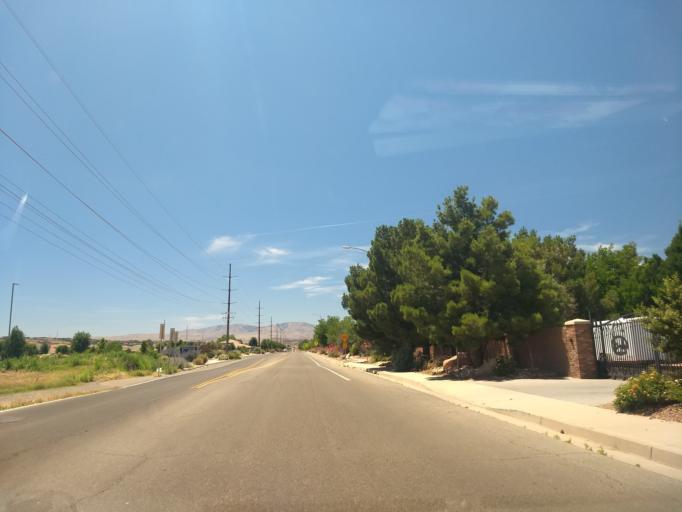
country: US
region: Utah
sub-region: Washington County
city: Washington
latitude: 37.0889
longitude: -113.5015
